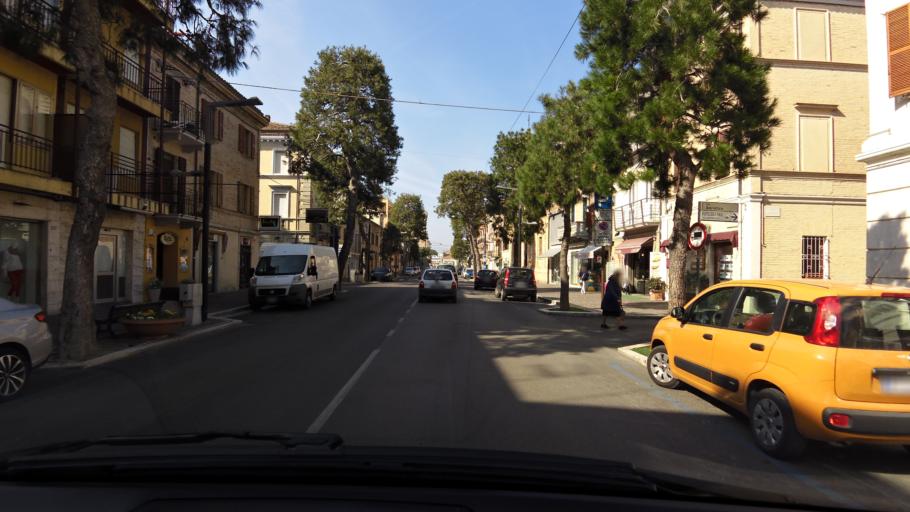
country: IT
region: The Marches
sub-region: Provincia di Macerata
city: Porto Recanati
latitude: 43.4338
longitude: 13.6632
